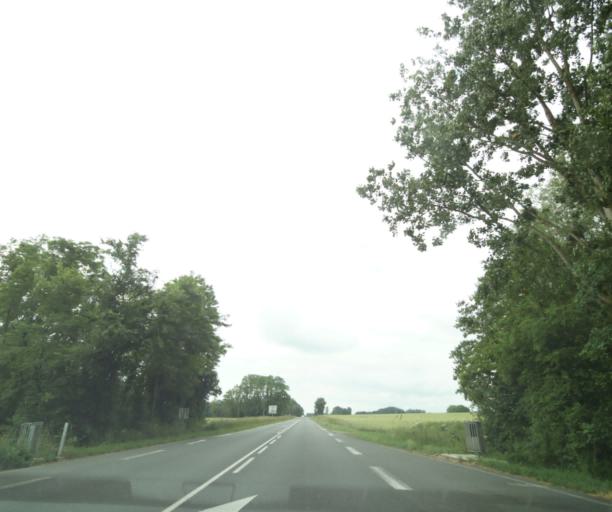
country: FR
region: Pays de la Loire
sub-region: Departement de Maine-et-Loire
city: Distre
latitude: 47.1910
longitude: -0.1280
